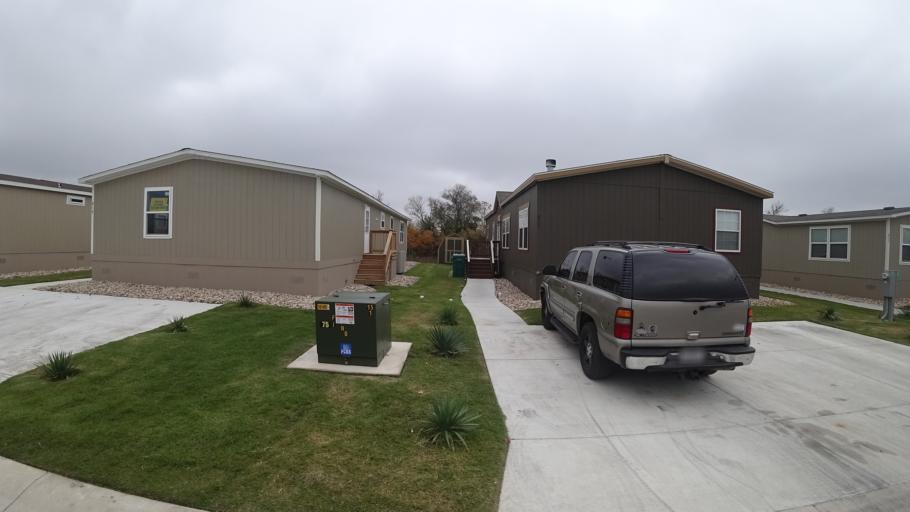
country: US
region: Texas
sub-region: Travis County
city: Pflugerville
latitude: 30.3905
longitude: -97.6370
